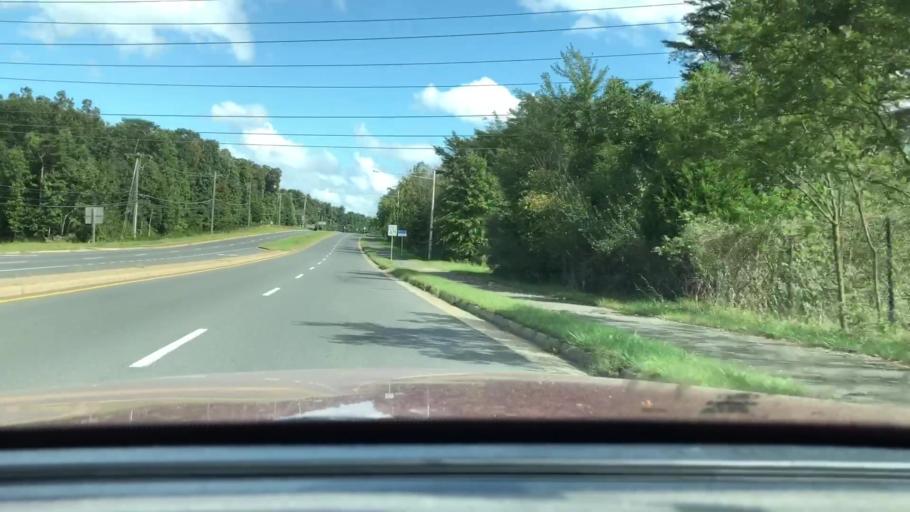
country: US
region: Virginia
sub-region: Fairfax County
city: Centreville
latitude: 38.8300
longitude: -77.4026
